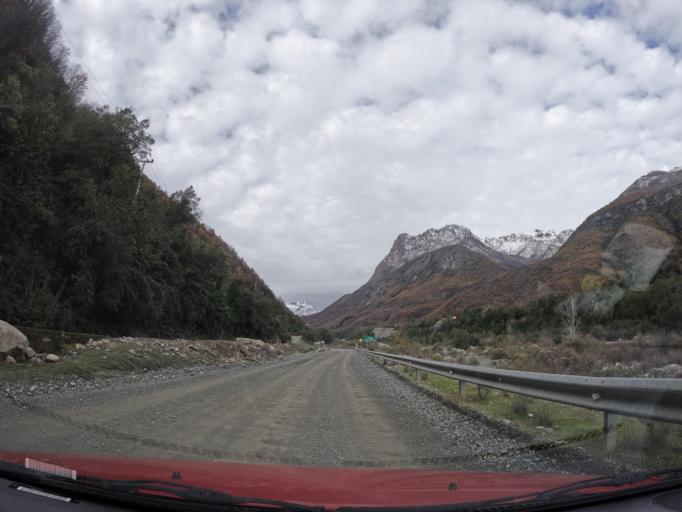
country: CL
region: Maule
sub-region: Provincia de Linares
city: Colbun
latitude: -35.8583
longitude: -71.2191
